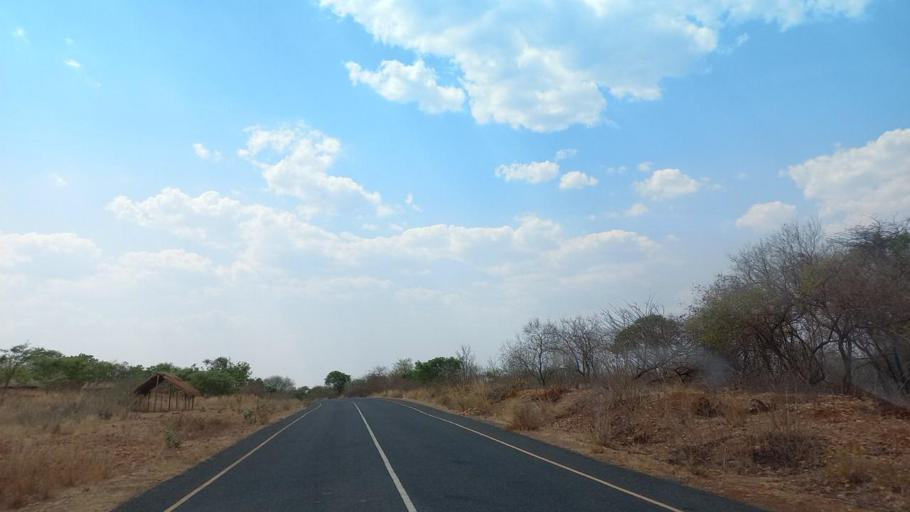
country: ZM
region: Lusaka
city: Luangwa
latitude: -15.3403
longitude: 30.3590
